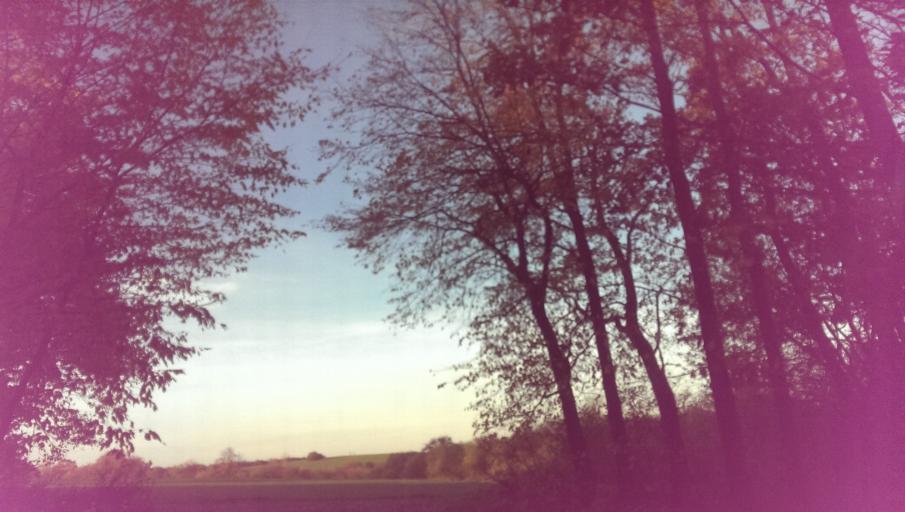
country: CZ
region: Zlin
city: Brezolupy
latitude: 49.1449
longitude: 17.5970
